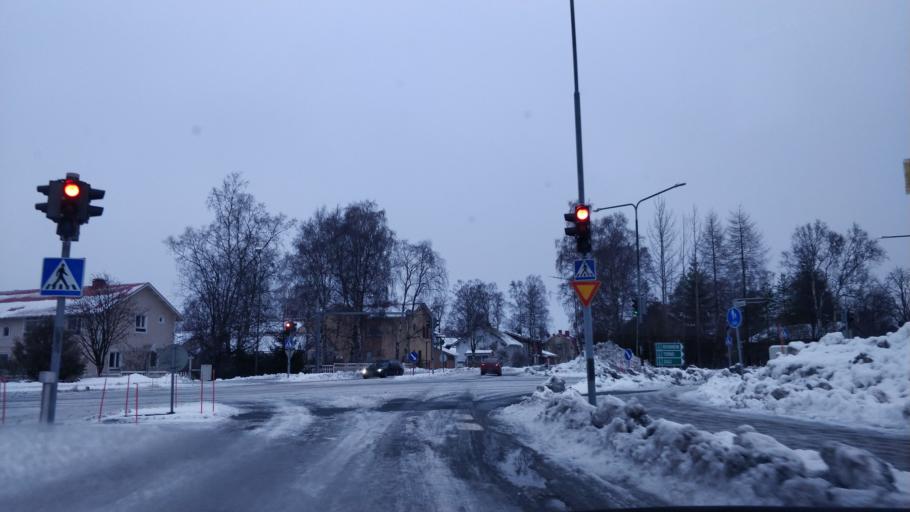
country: FI
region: Lapland
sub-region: Kemi-Tornio
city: Kemi
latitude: 65.7391
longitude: 24.5615
